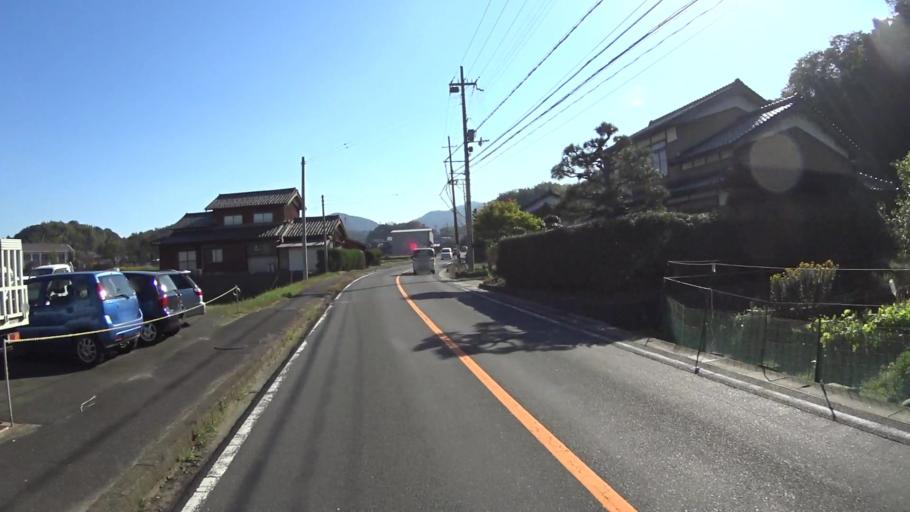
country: JP
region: Kyoto
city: Miyazu
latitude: 35.6555
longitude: 135.0326
